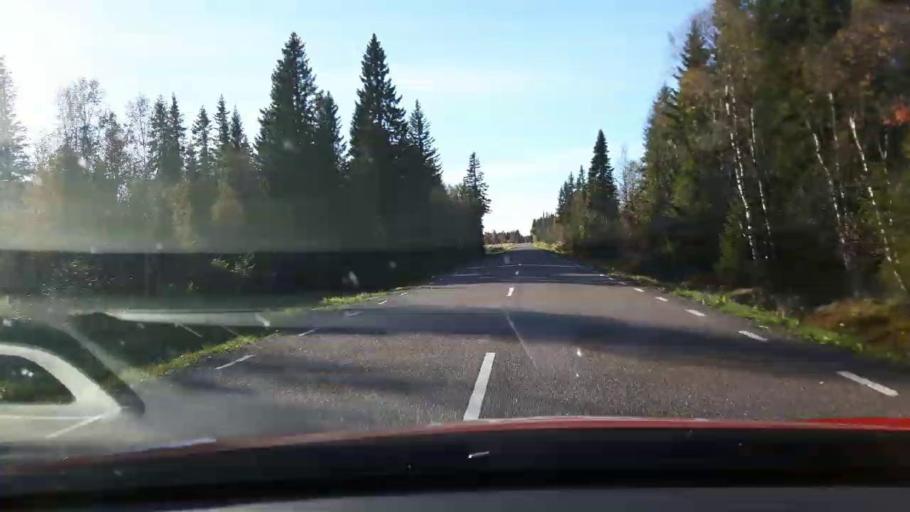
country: SE
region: Jaemtland
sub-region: Stroemsunds Kommun
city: Stroemsund
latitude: 63.8621
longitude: 15.1677
